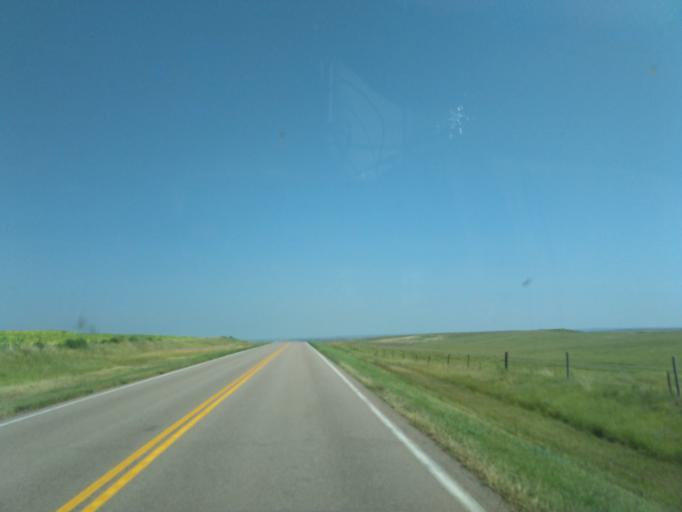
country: US
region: Nebraska
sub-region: Dundy County
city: Benkelman
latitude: 39.9536
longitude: -101.5415
